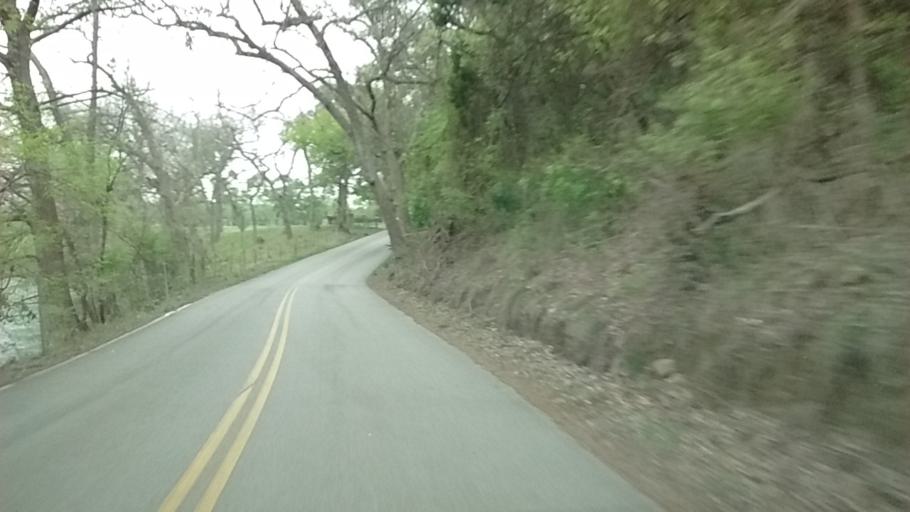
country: US
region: Texas
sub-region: Comal County
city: Canyon Lake
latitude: 29.8086
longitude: -98.1730
